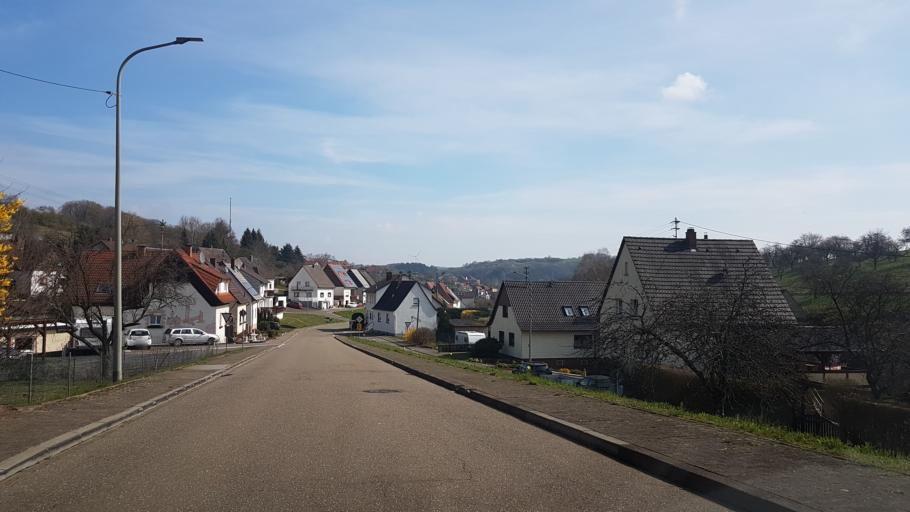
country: DE
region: Rheinland-Pfalz
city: Altenkirchen
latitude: 49.4404
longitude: 7.3084
